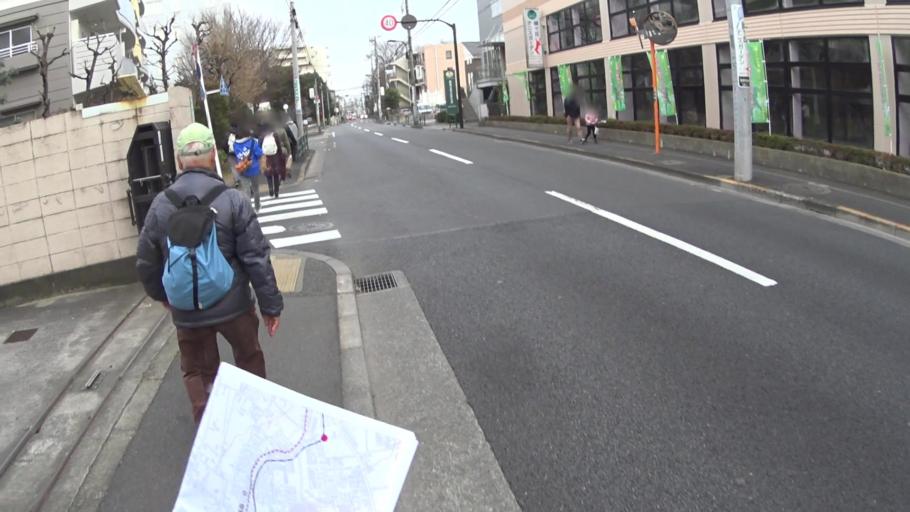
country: JP
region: Tokyo
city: Mitaka-shi
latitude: 35.6721
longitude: 139.5874
